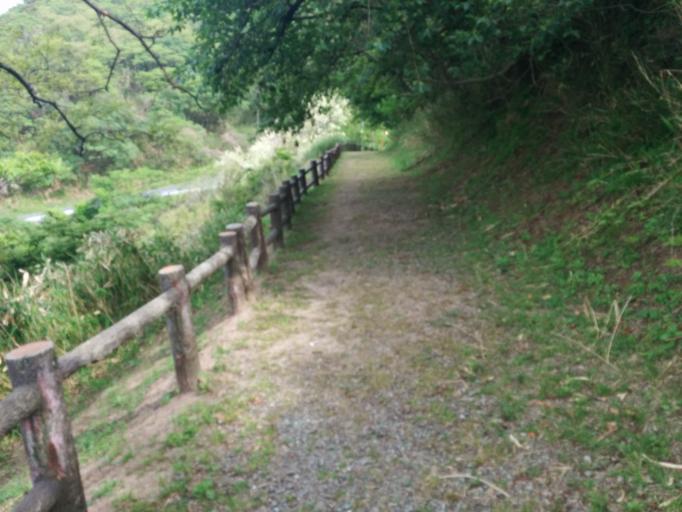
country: JP
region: Hyogo
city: Toyooka
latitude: 35.6928
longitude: 135.0032
